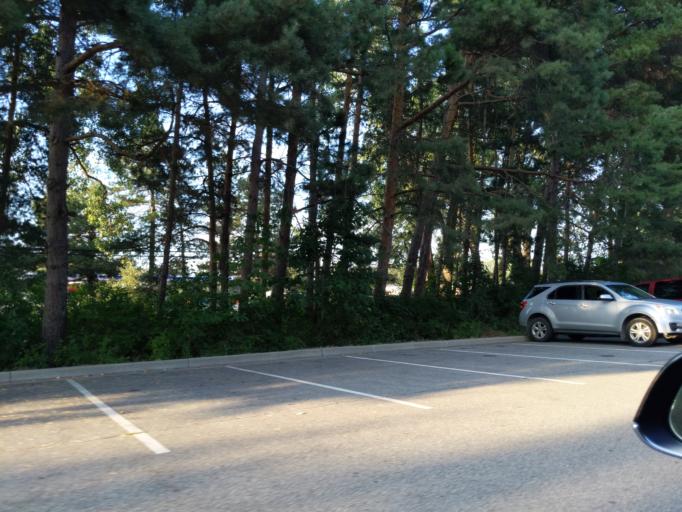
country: US
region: Michigan
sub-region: Isabella County
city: Mount Pleasant
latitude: 43.5966
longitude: -84.7926
